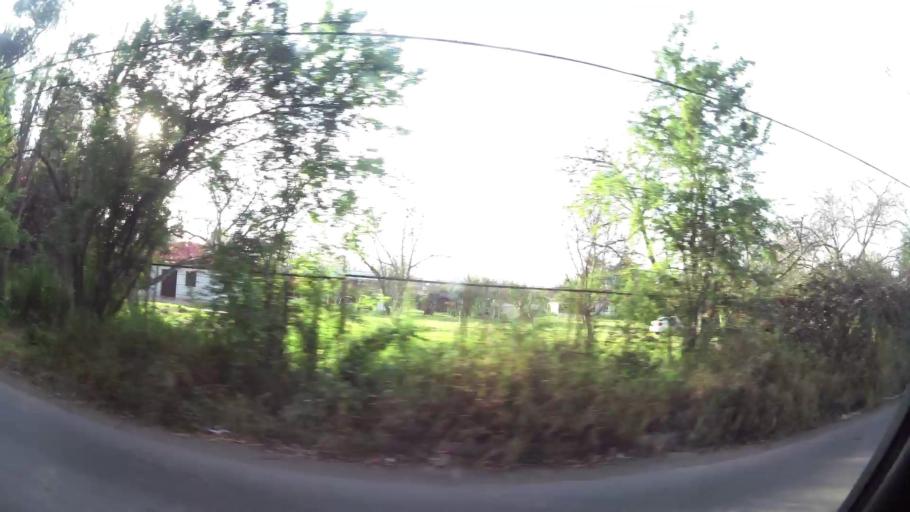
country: CL
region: Santiago Metropolitan
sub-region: Provincia de Maipo
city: San Bernardo
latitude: -33.5591
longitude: -70.7719
